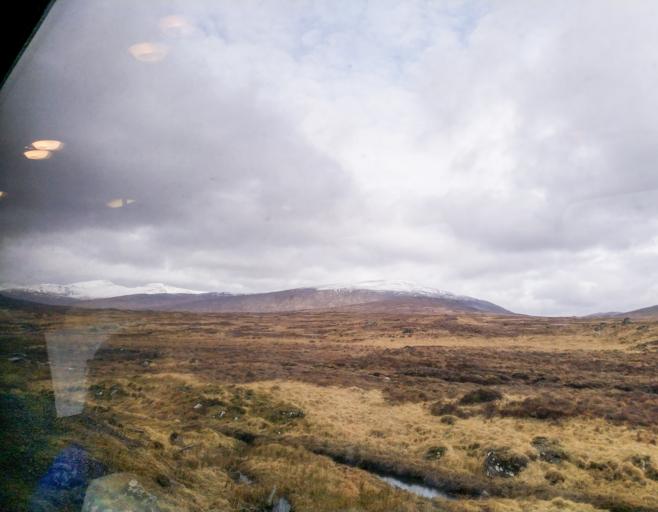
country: GB
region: Scotland
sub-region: Highland
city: Spean Bridge
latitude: 56.7289
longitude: -4.6440
